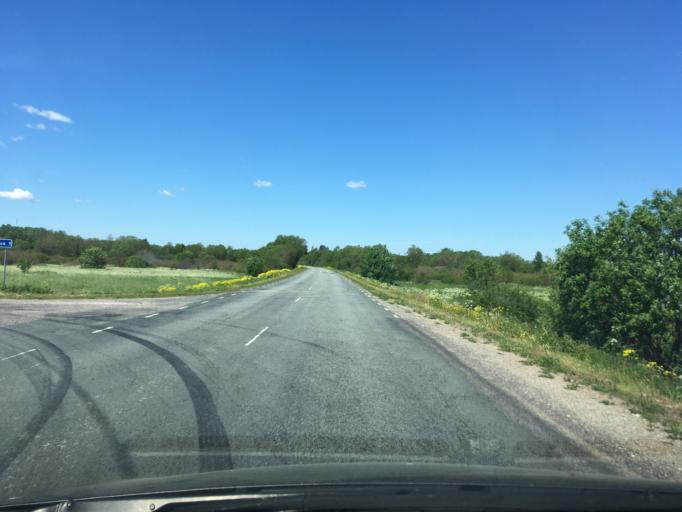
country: EE
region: Harju
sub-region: Rae vald
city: Vaida
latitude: 59.1885
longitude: 25.0068
